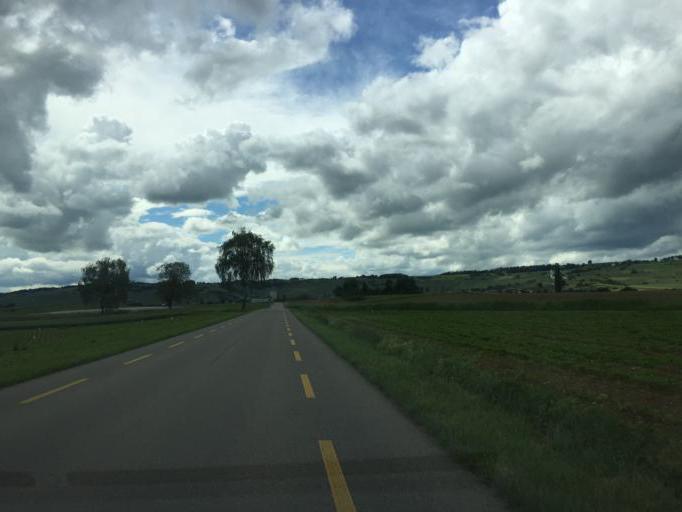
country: CH
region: Schaffhausen
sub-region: Bezirk Oberklettgau
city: Neunkirch
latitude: 47.6913
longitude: 8.4858
